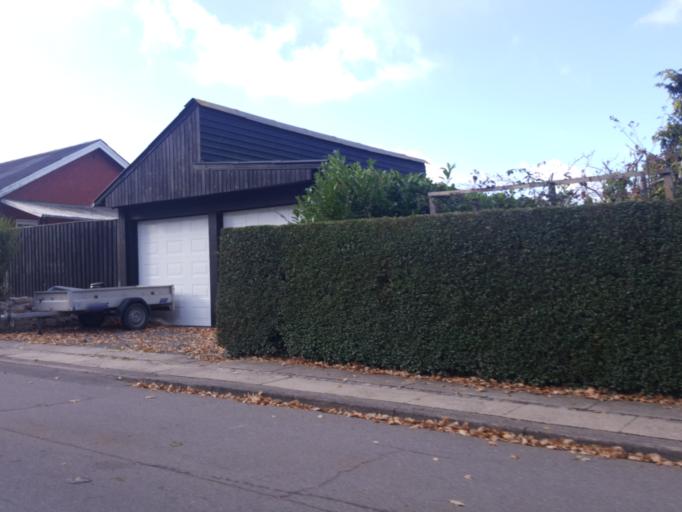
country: DK
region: Zealand
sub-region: Kalundborg Kommune
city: Kalundborg
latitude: 55.6897
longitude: 11.0801
